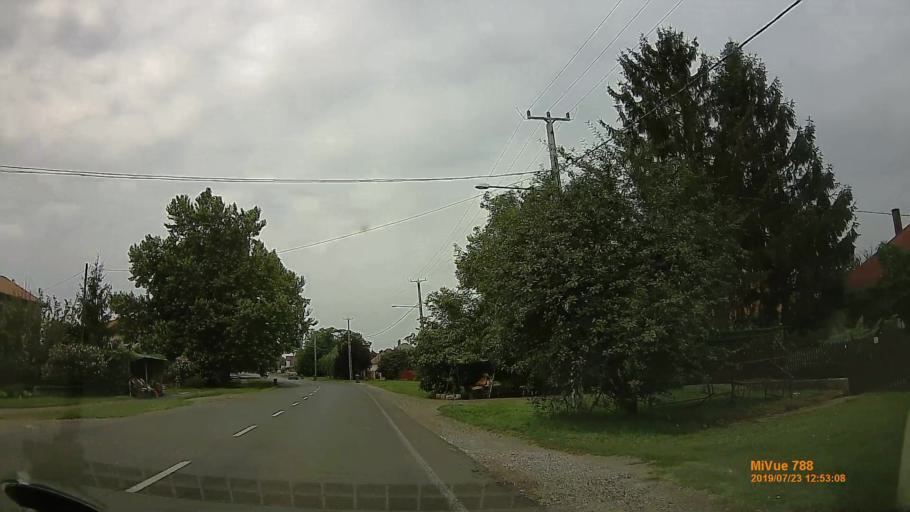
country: HU
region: Szabolcs-Szatmar-Bereg
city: Nagycserkesz
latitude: 47.9627
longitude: 21.5576
